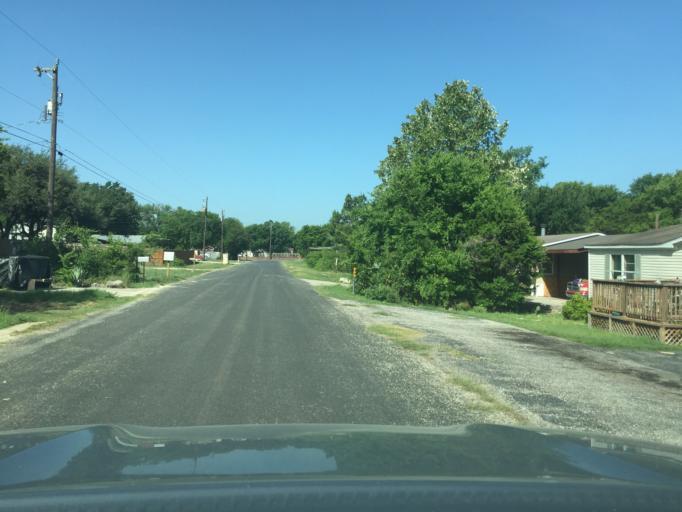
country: US
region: Texas
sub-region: Bexar County
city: Timberwood Park
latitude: 29.7049
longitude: -98.4777
